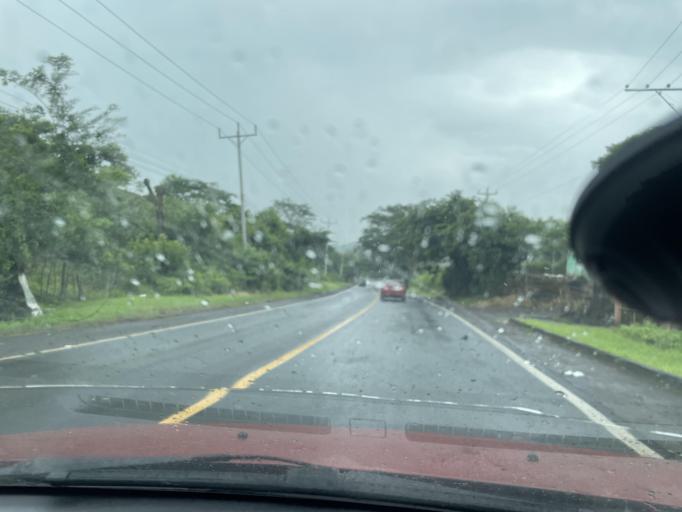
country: SV
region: San Miguel
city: San Miguel
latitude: 13.5418
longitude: -88.1268
